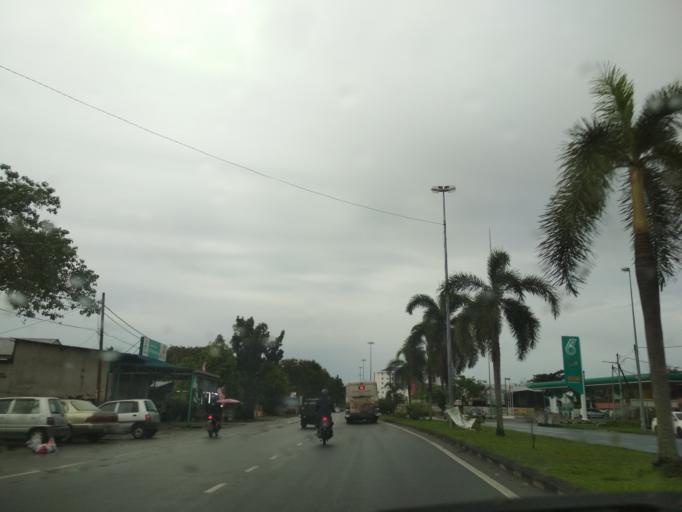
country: MY
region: Perlis
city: Kangar
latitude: 6.4279
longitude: 100.1849
